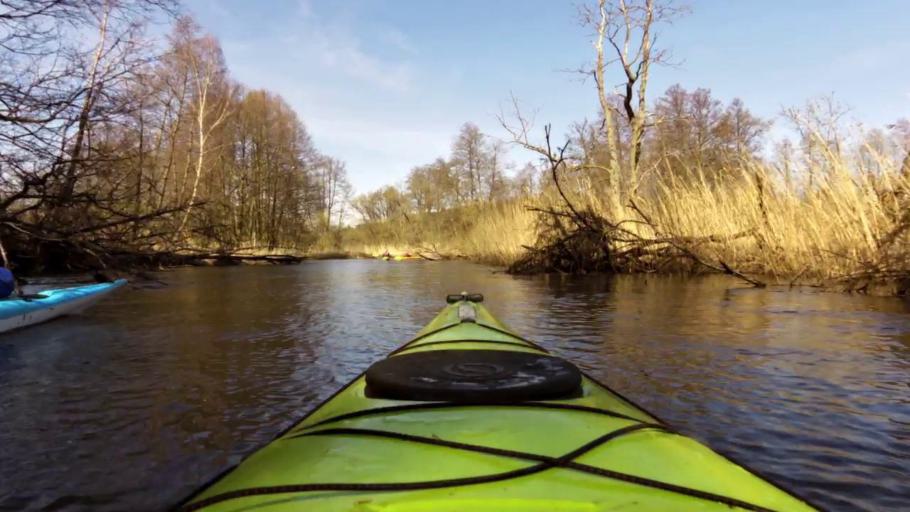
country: PL
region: West Pomeranian Voivodeship
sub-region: Powiat lobeski
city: Lobez
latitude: 53.6790
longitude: 15.5616
